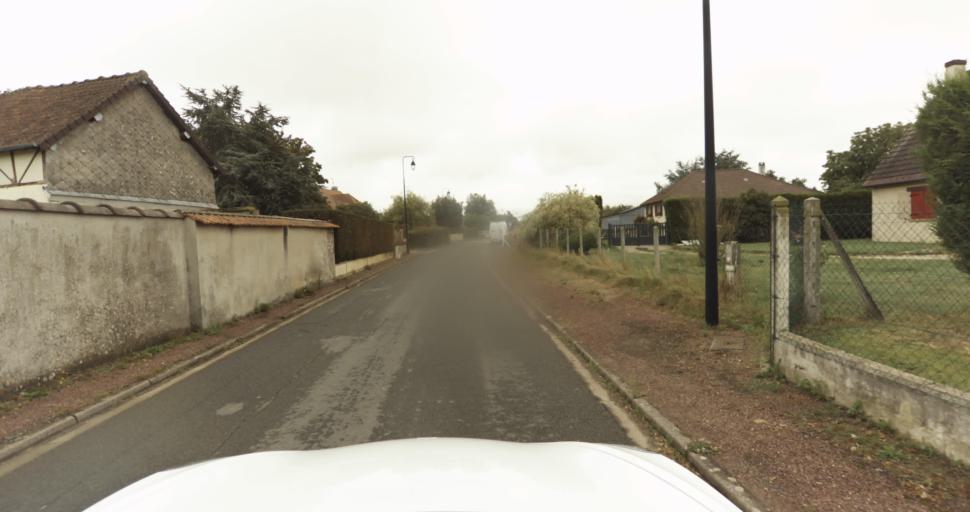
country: FR
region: Haute-Normandie
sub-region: Departement de l'Eure
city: Aviron
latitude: 49.0766
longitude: 1.0886
